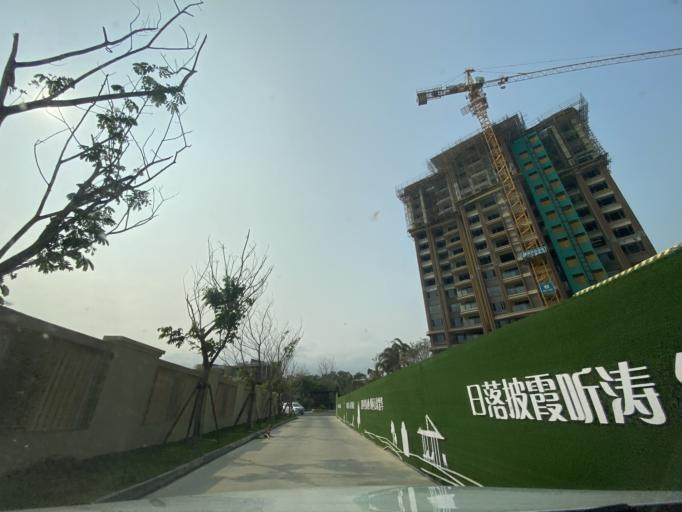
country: CN
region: Hainan
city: Yingzhou
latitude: 18.3936
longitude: 109.8542
